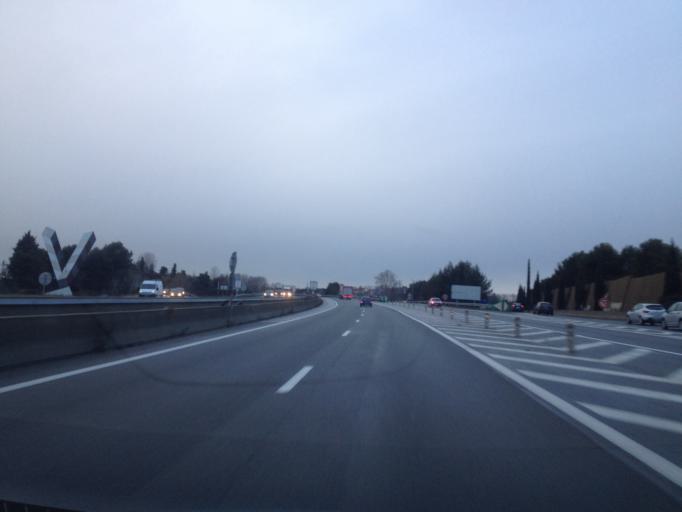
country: FR
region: Provence-Alpes-Cote d'Azur
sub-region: Departement des Bouches-du-Rhone
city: Aix-en-Provence
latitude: 43.5177
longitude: 5.4306
